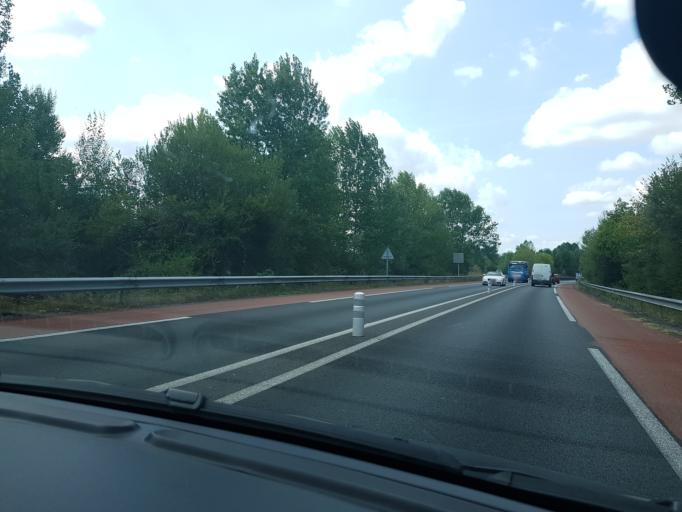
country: FR
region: Aquitaine
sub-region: Departement de la Gironde
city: Arveyres
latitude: 44.8701
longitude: -0.2763
